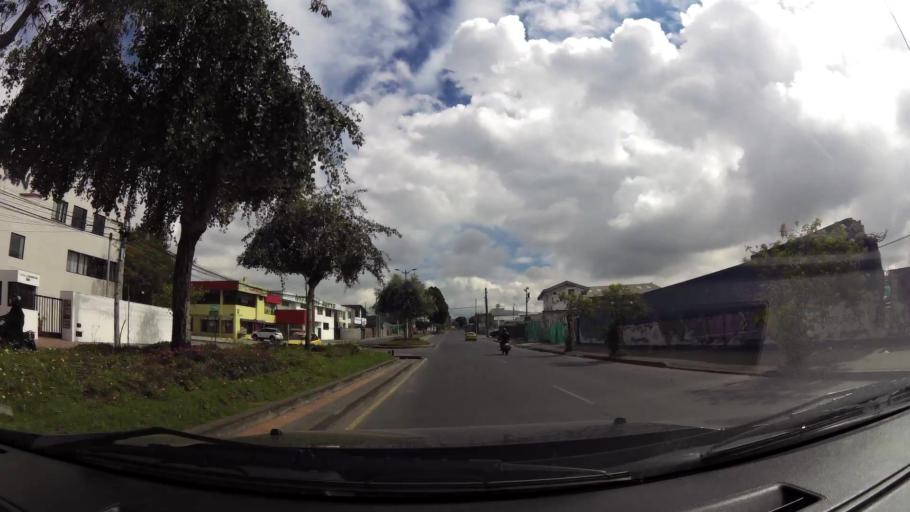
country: EC
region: Pichincha
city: Quito
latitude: -0.1527
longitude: -78.4883
